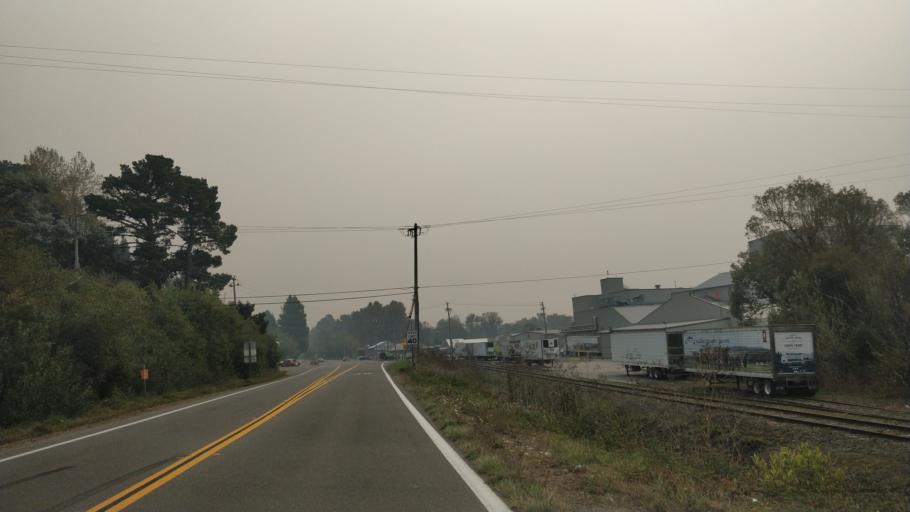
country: US
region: California
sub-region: Humboldt County
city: Fortuna
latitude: 40.6174
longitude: -124.2039
